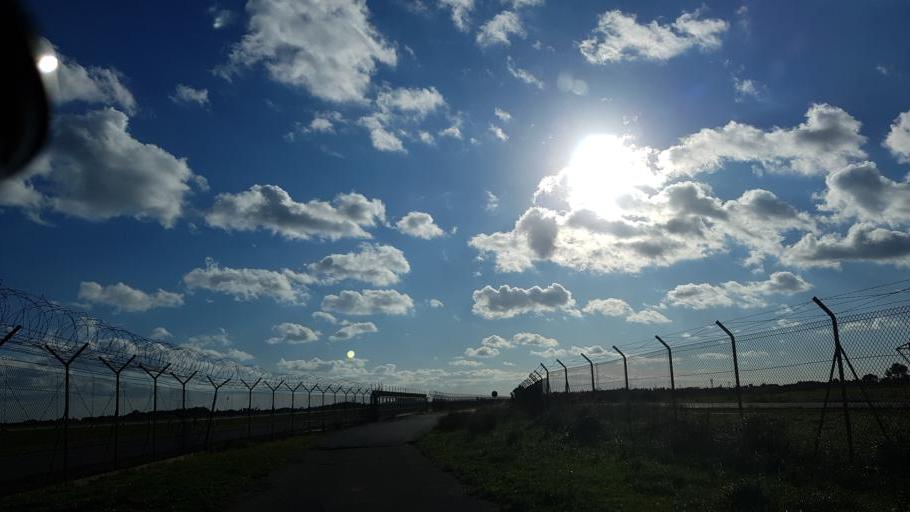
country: IT
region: Apulia
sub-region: Provincia di Brindisi
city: Materdomini
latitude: 40.6738
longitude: 17.9250
